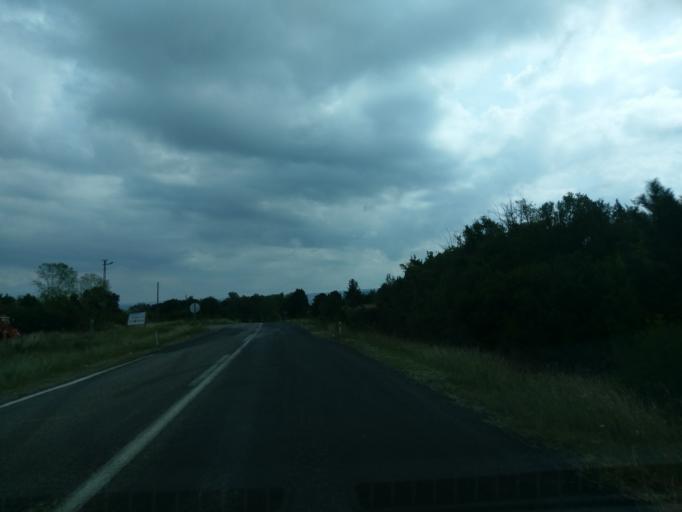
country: TR
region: Sinop
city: Ayancik
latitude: 41.9446
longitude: 34.6892
